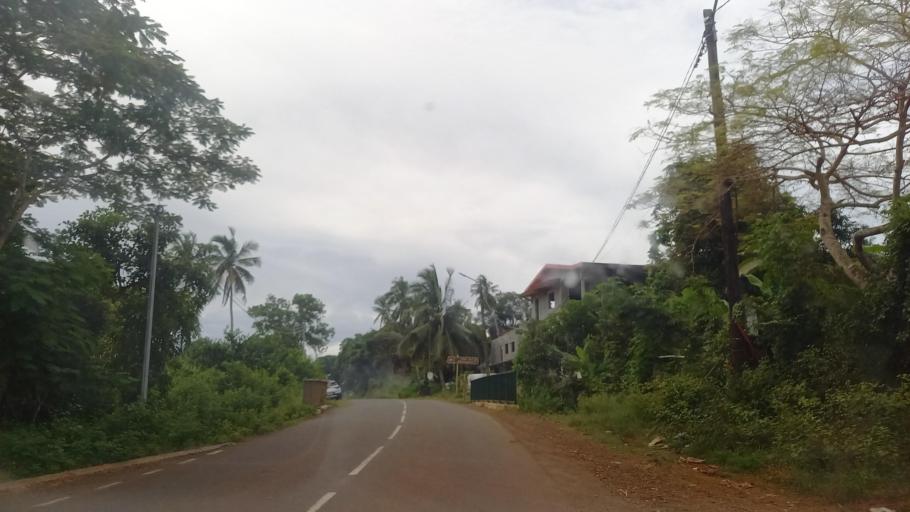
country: YT
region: Kani-Keli
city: Kani Keli
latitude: -12.9394
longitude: 45.1022
